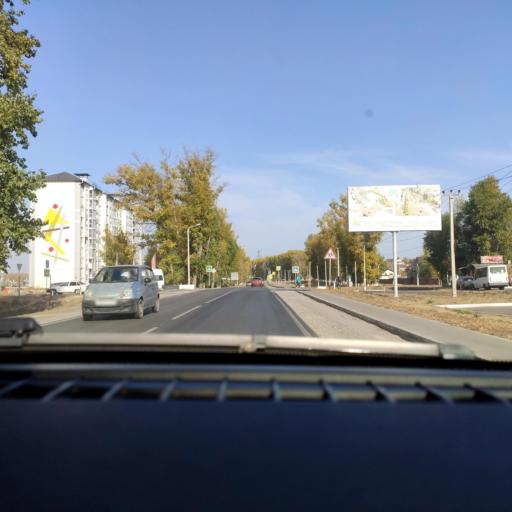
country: RU
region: Voronezj
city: Novaya Usman'
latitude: 51.6695
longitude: 39.4057
